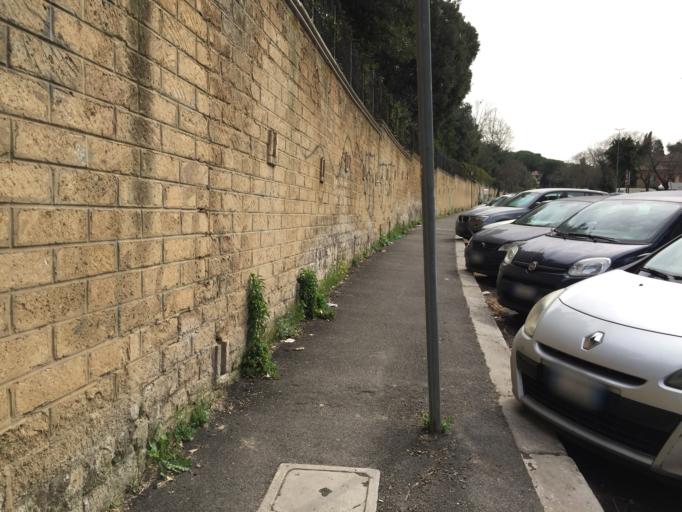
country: VA
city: Vatican City
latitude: 41.8937
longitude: 12.4584
